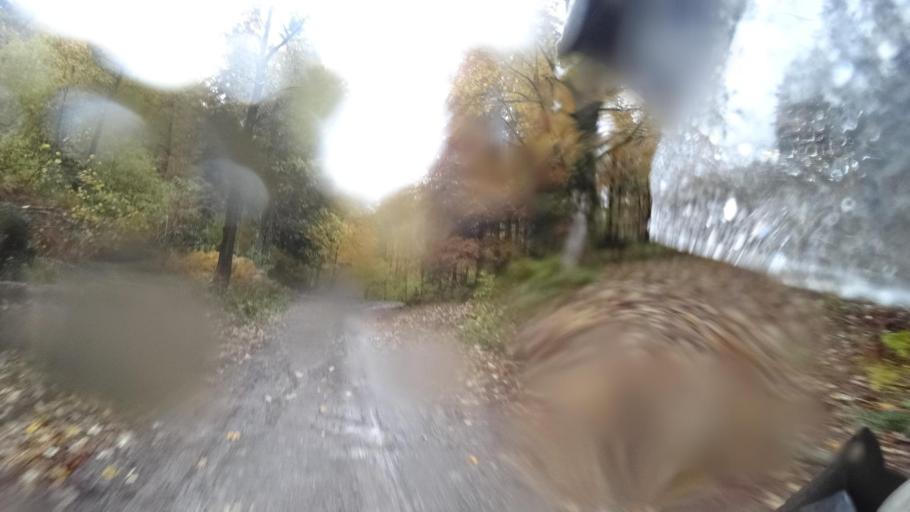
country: HR
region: Primorsko-Goranska
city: Vrbovsko
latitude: 45.3127
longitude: 15.0734
